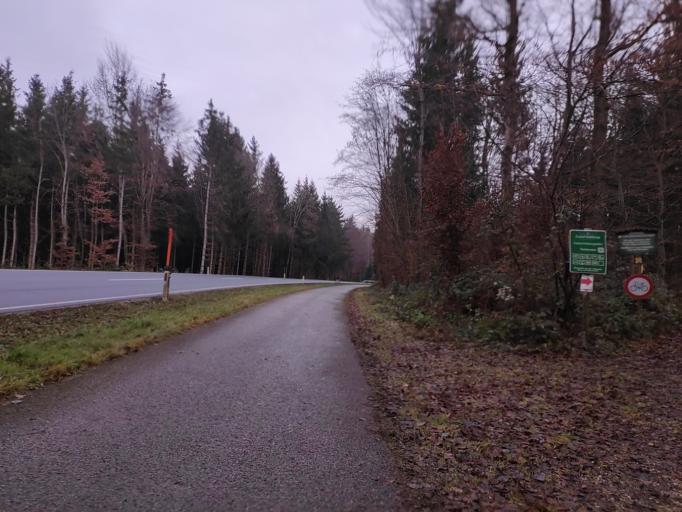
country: AT
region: Salzburg
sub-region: Politischer Bezirk Salzburg-Umgebung
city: Mattsee
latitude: 47.9863
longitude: 13.1053
